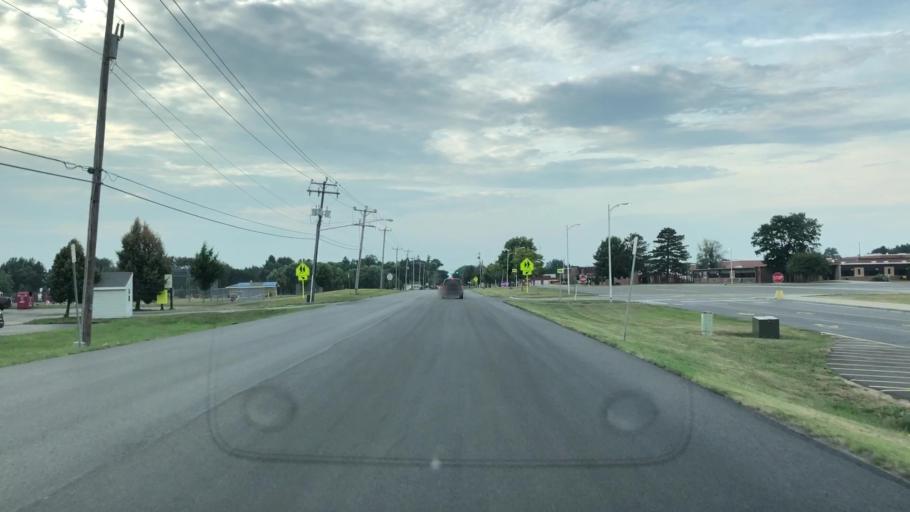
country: US
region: New York
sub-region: Erie County
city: Elma Center
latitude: 42.8329
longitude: -78.6060
